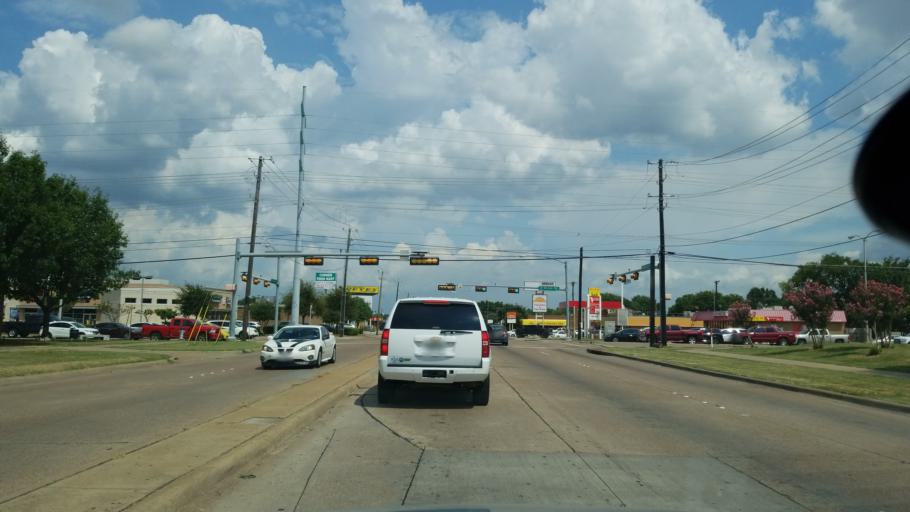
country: US
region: Texas
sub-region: Dallas County
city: Garland
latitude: 32.9164
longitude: -96.6660
